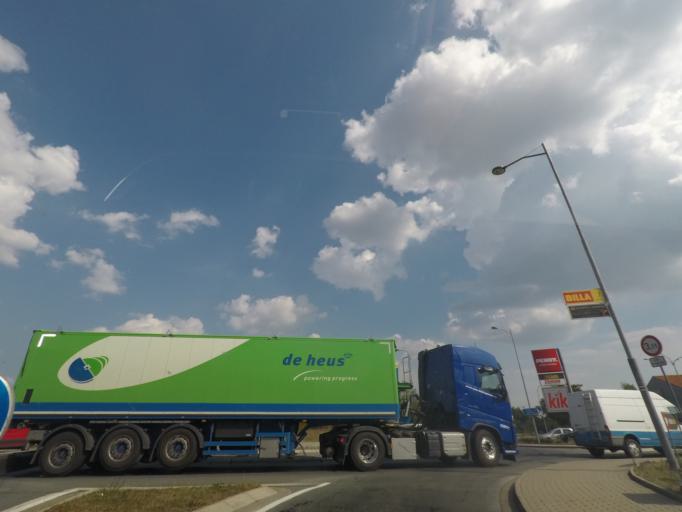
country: CZ
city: Tyniste nad Orlici
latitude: 50.1484
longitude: 16.0693
